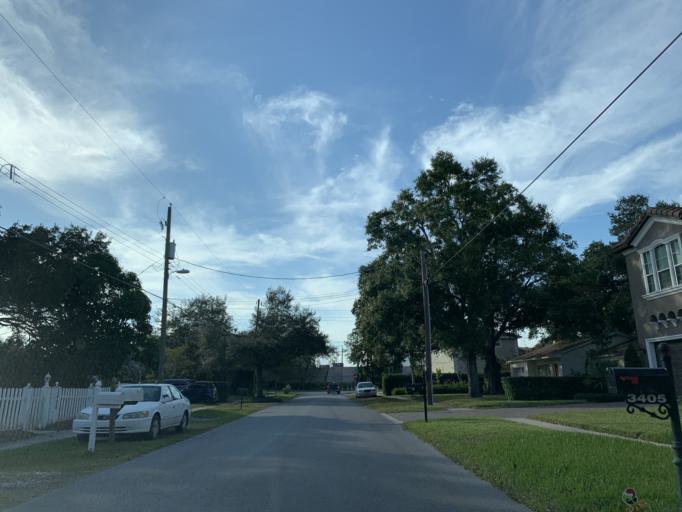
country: US
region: Florida
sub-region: Hillsborough County
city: Tampa
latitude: 27.9015
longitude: -82.5011
